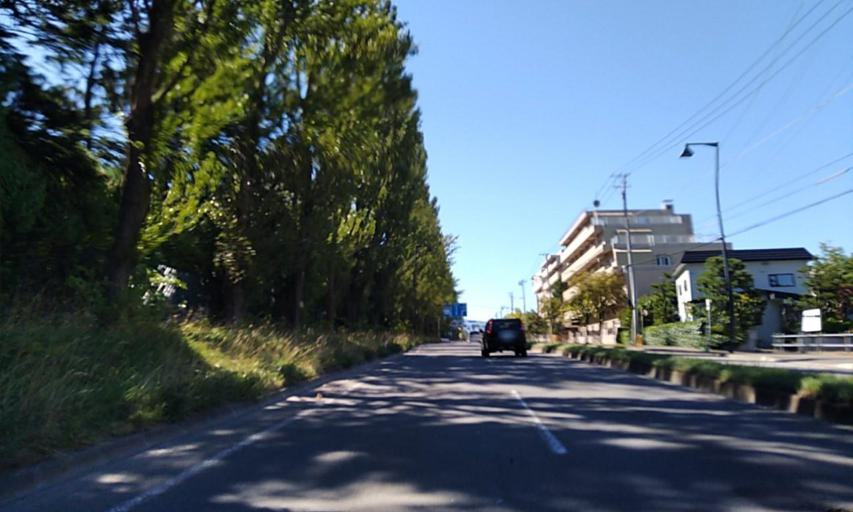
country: JP
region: Hokkaido
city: Sapporo
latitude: 43.0152
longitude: 141.4062
